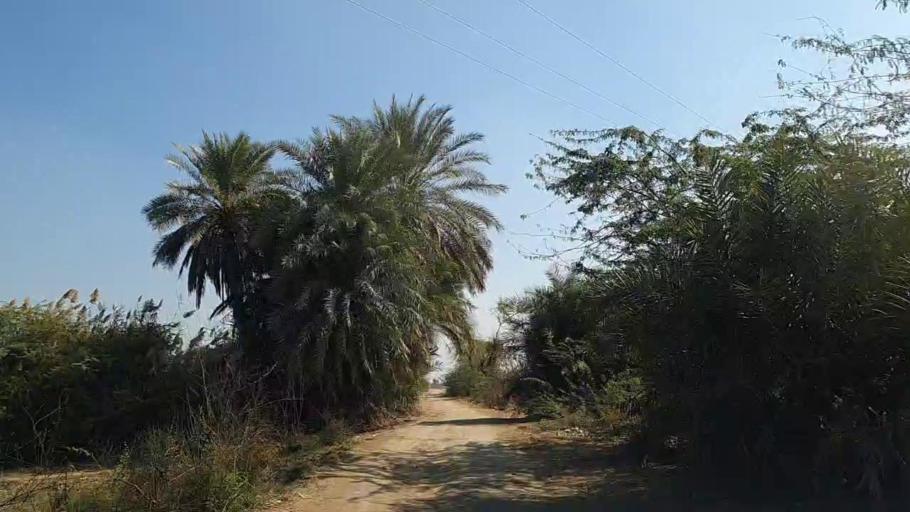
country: PK
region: Sindh
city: Daur
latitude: 26.4821
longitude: 68.3316
